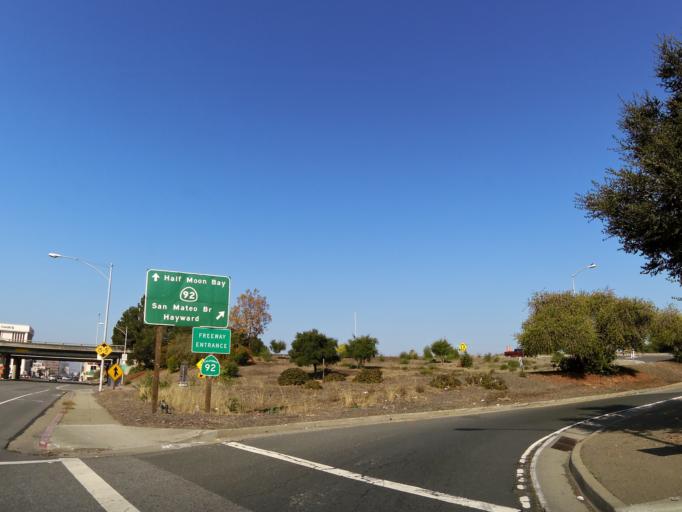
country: US
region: California
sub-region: San Mateo County
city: San Mateo
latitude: 37.5495
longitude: -122.3110
